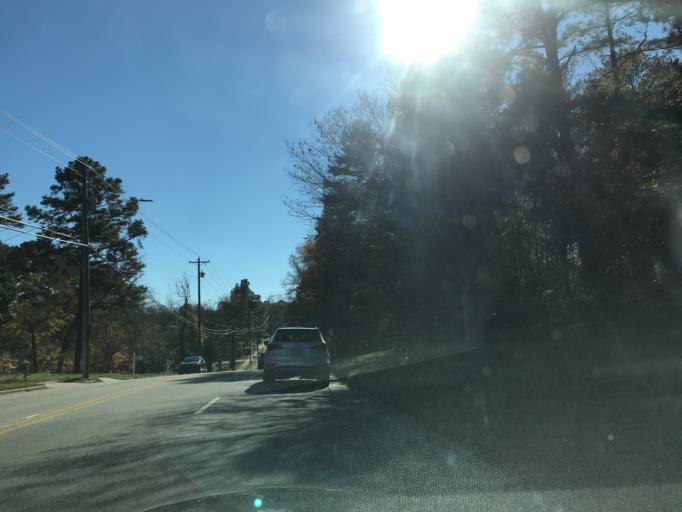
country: US
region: North Carolina
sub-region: Wake County
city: Raleigh
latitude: 35.8326
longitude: -78.6027
